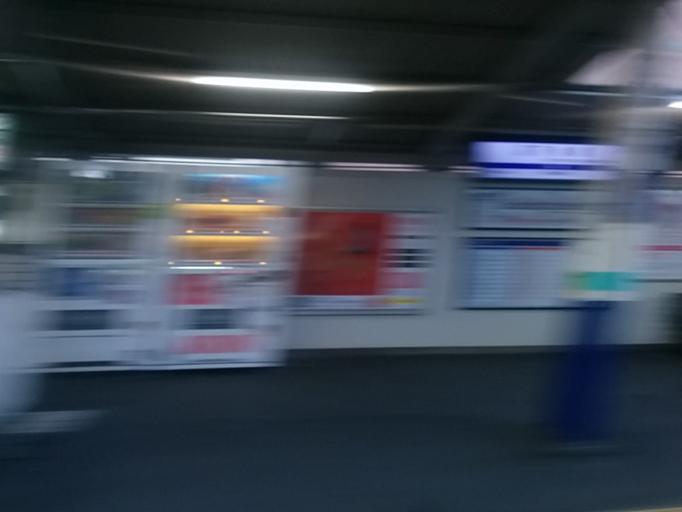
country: JP
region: Saitama
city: Wako
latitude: 35.7704
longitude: 139.6447
